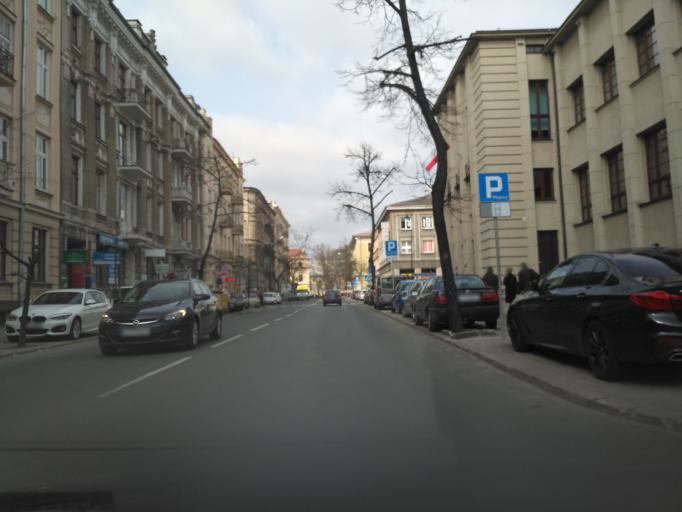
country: PL
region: Lublin Voivodeship
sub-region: Powiat lubelski
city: Lublin
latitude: 51.2462
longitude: 22.5541
